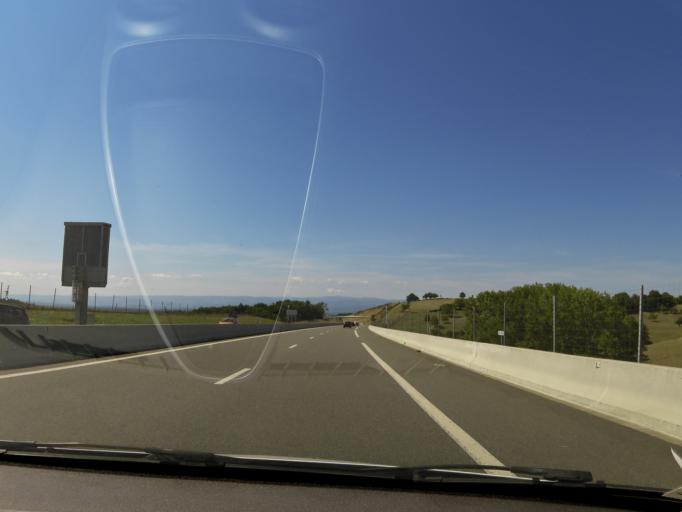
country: FR
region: Rhone-Alpes
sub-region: Departement de la Loire
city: Balbigny
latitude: 45.8487
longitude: 4.2195
